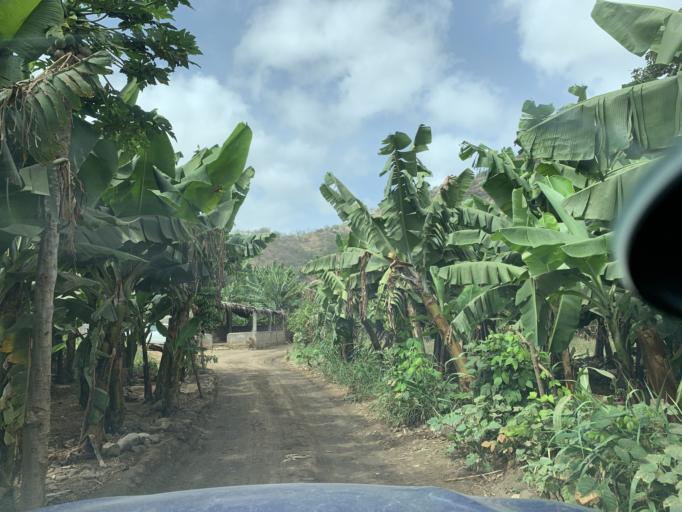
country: CV
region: Santa Cruz
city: Santa Cruz
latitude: 15.1128
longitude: -23.5642
